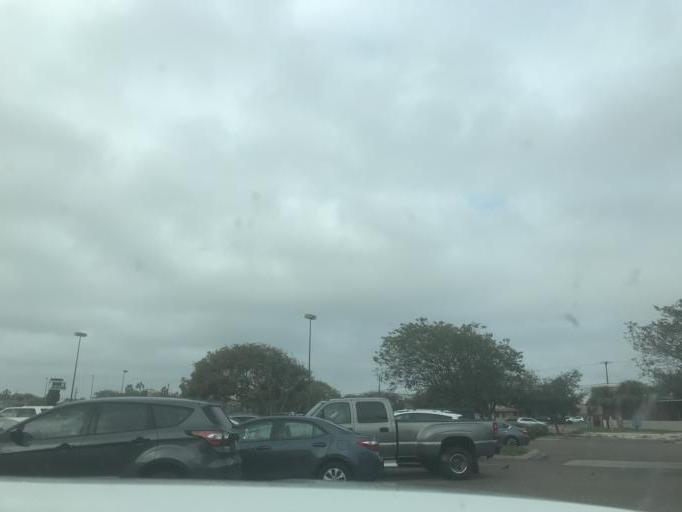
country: US
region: Texas
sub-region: Nueces County
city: Corpus Christi
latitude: 27.6847
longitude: -97.3854
